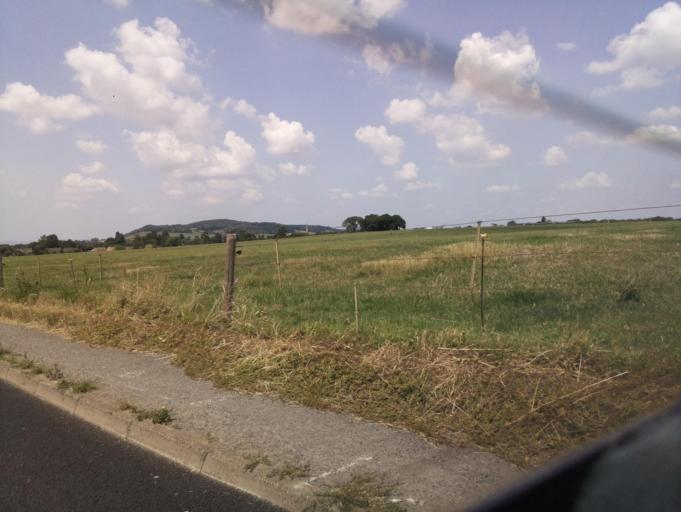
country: GB
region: England
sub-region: Gloucestershire
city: Winchcombe
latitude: 51.9903
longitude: -1.9406
